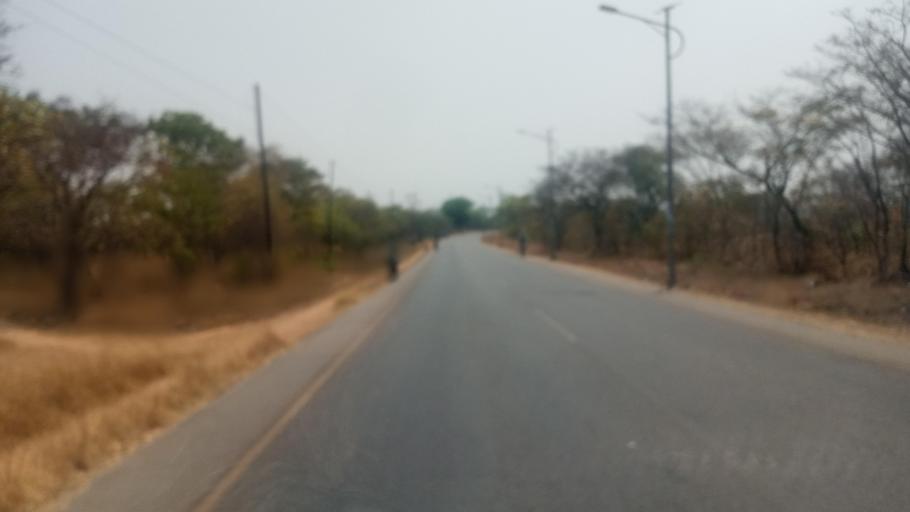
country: ZM
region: Lusaka
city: Lusaka
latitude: -15.4706
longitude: 28.4270
